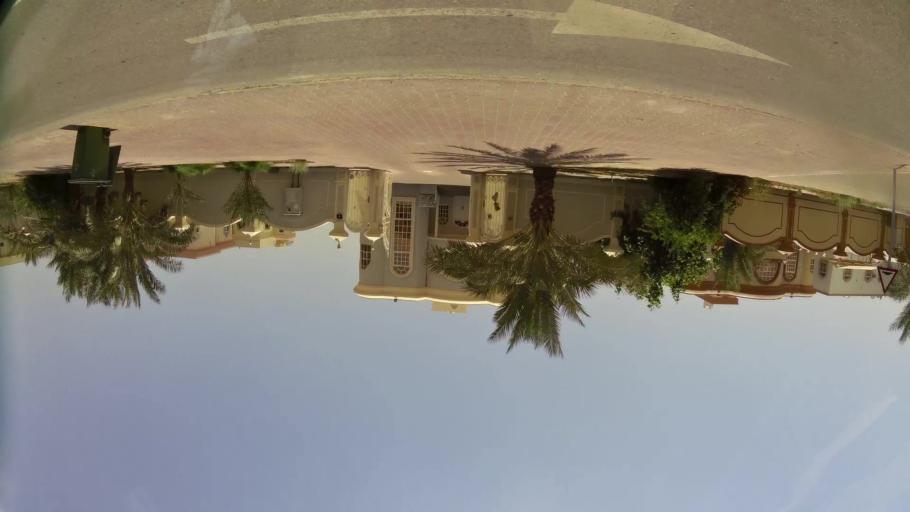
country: AE
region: Ajman
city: Ajman
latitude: 25.4220
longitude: 55.5100
